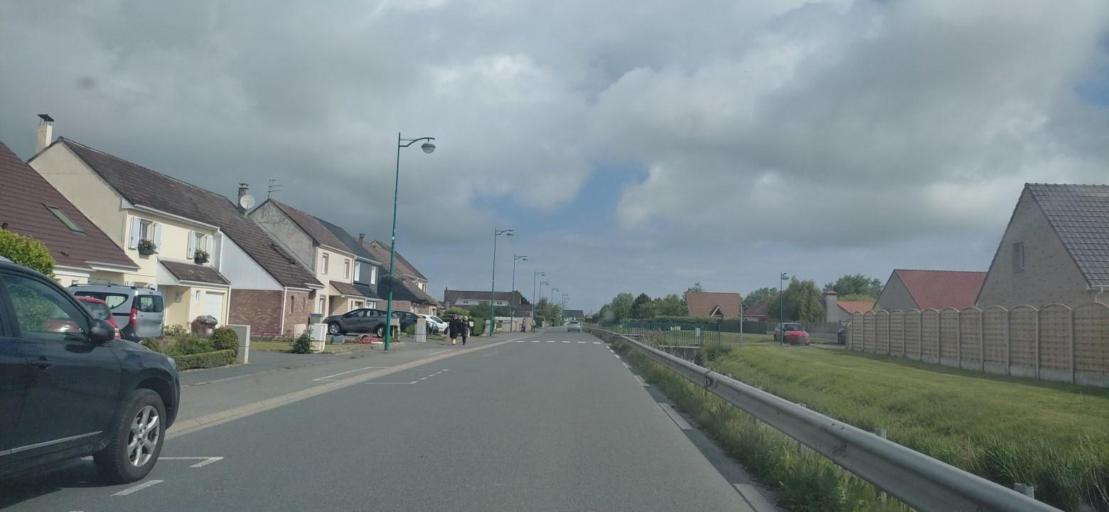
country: FR
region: Nord-Pas-de-Calais
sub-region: Departement du Pas-de-Calais
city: Oye-Plage
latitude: 50.9825
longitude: 2.0370
